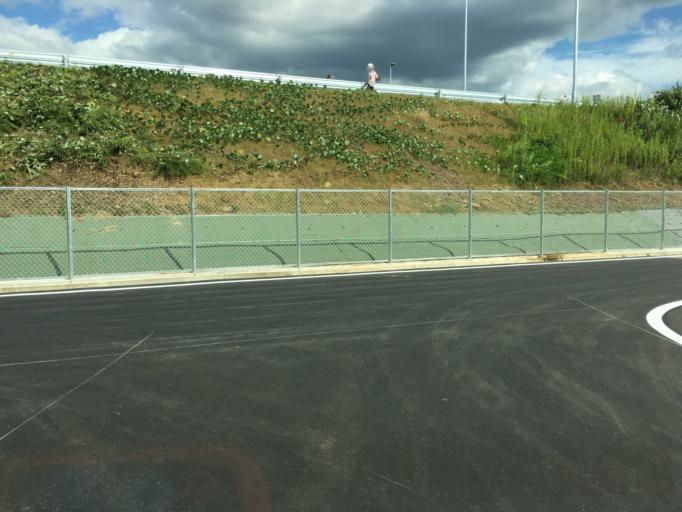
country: JP
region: Fukushima
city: Fukushima-shi
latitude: 37.7908
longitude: 140.4147
